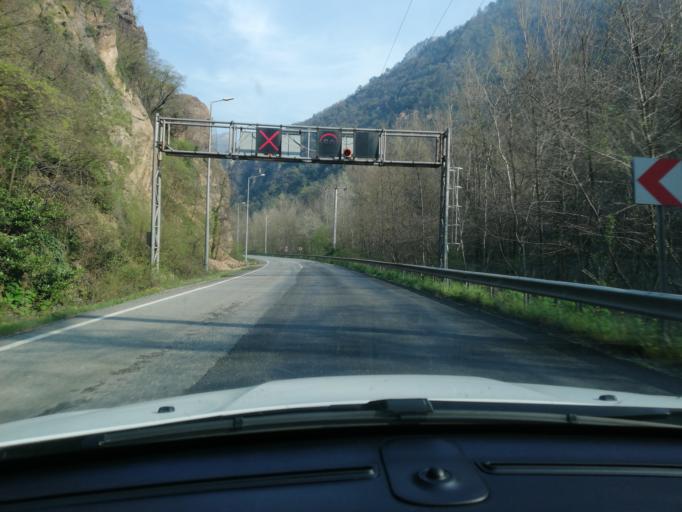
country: TR
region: Karabuk
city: Yenice
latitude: 41.1811
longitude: 32.4483
